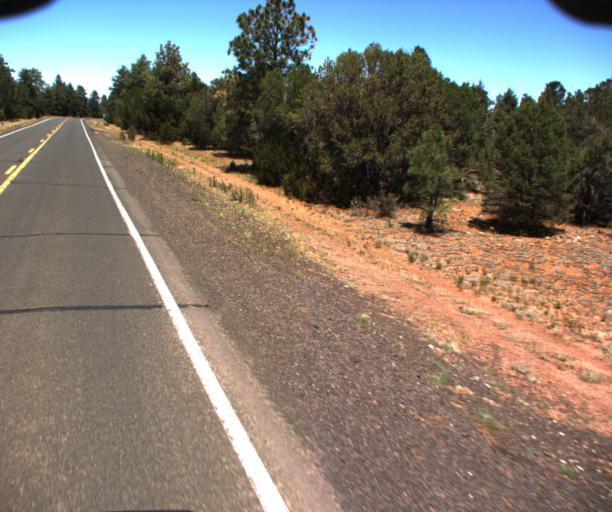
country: US
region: Arizona
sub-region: Gila County
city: Star Valley
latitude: 34.6802
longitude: -111.1124
